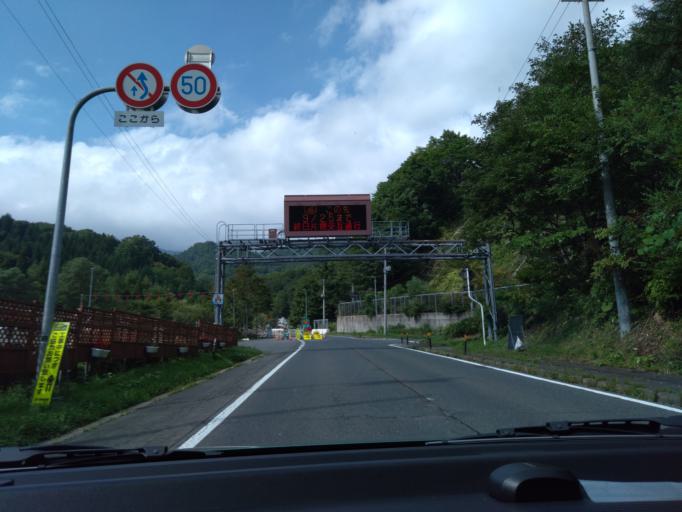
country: JP
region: Iwate
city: Shizukuishi
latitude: 39.7233
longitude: 140.8406
